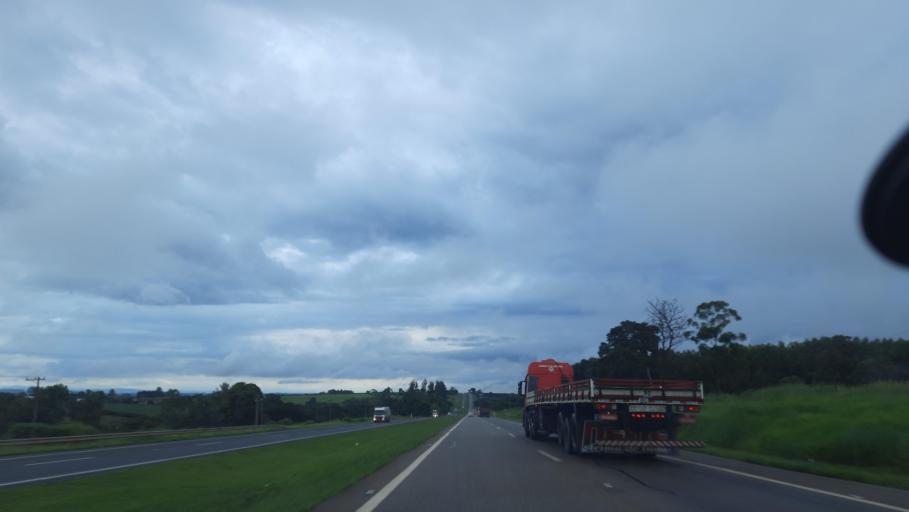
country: BR
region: Sao Paulo
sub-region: Moji-Guacu
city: Mogi-Gaucu
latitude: -22.2339
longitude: -46.9786
